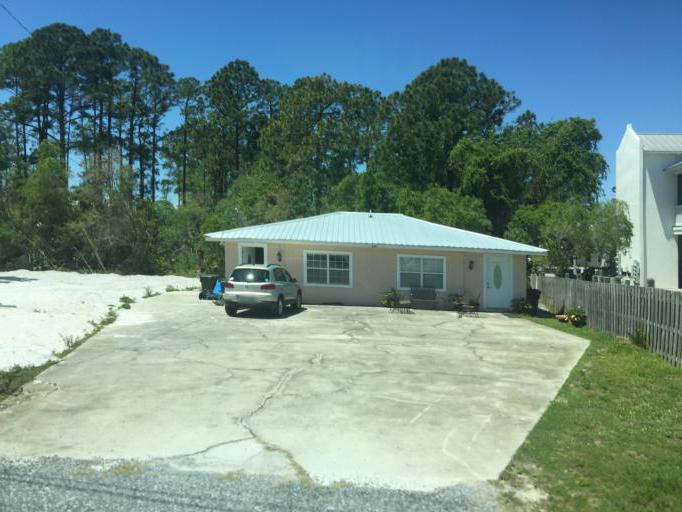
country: US
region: Florida
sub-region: Bay County
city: Laguna Beach
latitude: 30.2632
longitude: -85.9685
